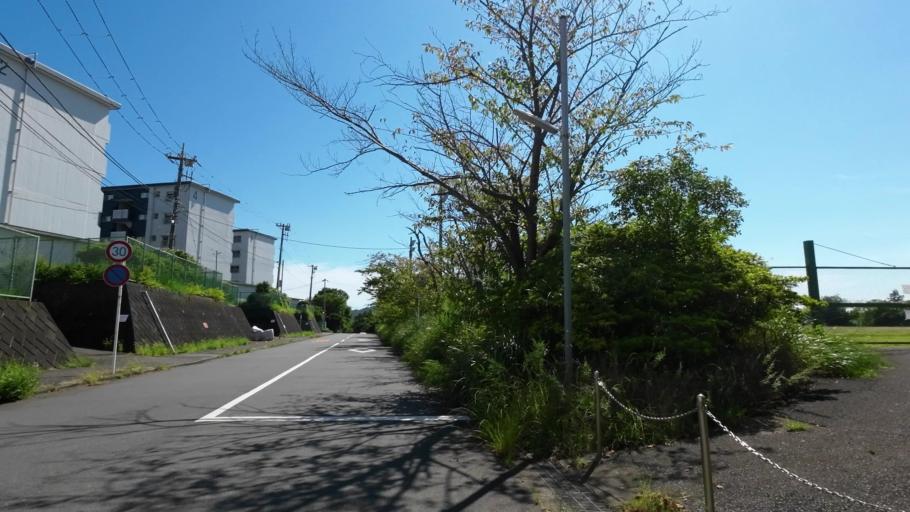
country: JP
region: Kanagawa
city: Kamakura
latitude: 35.3373
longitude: 139.5196
